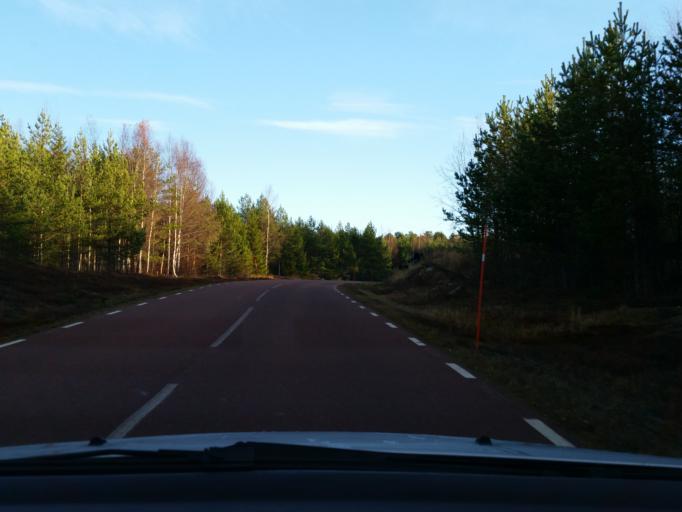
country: AX
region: Alands landsbygd
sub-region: Sund
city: Sund
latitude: 60.2804
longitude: 20.1082
